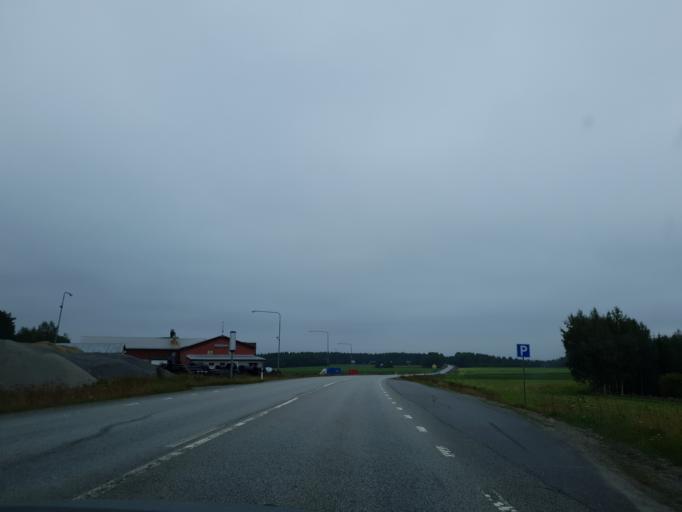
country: SE
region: Vaesterbotten
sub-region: Robertsfors Kommun
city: Robertsfors
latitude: 64.2331
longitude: 21.0179
